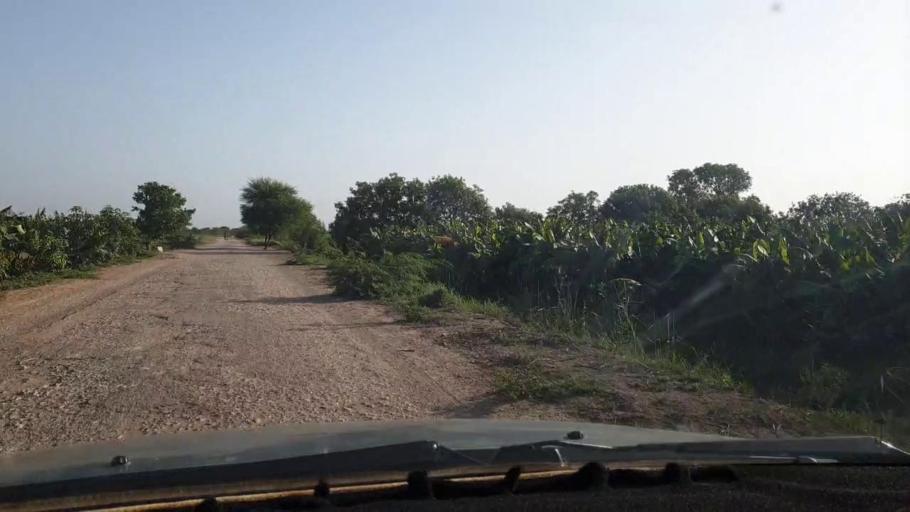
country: PK
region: Sindh
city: Mirwah Gorchani
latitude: 25.3016
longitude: 68.9643
